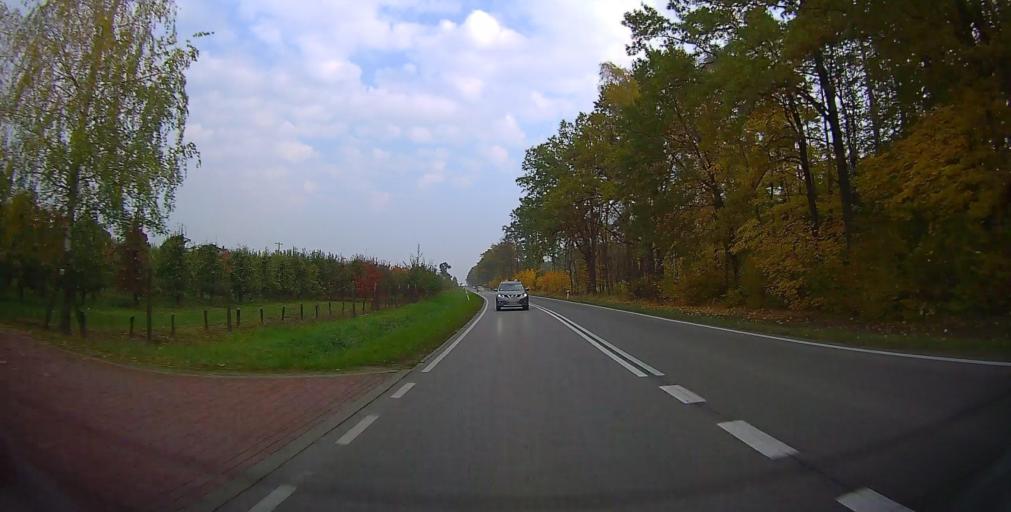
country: PL
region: Masovian Voivodeship
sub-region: Powiat grojecki
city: Belsk Duzy
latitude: 51.7920
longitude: 20.7838
